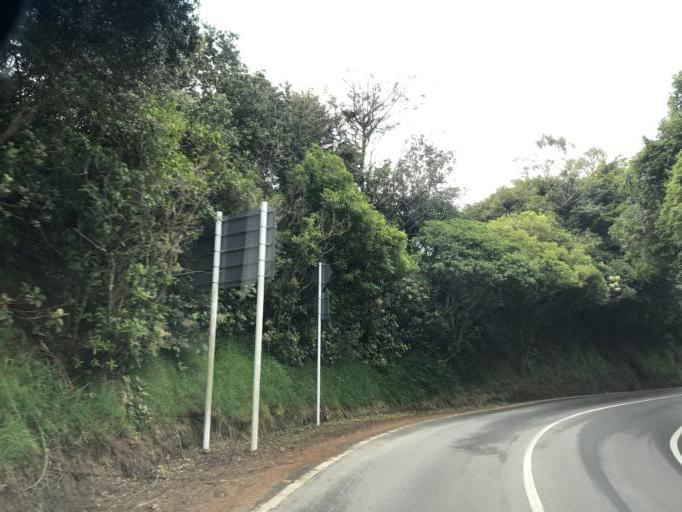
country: NZ
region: Wellington
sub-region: Wellington City
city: Kelburn
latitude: -41.2095
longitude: 174.7745
